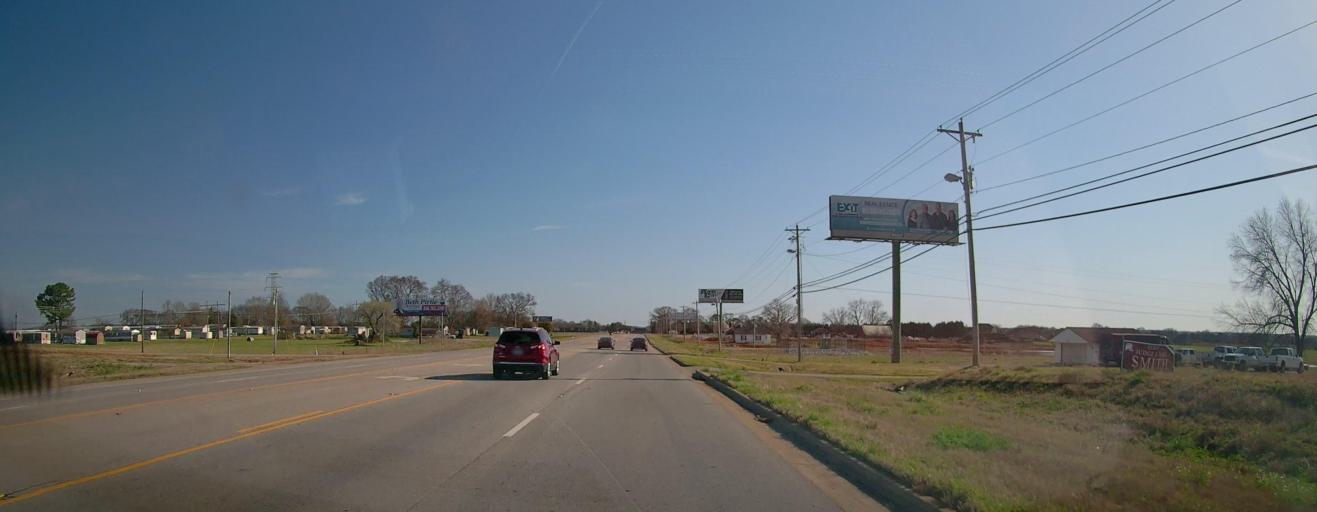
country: US
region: Alabama
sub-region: Colbert County
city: Muscle Shoals
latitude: 34.7231
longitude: -87.6351
